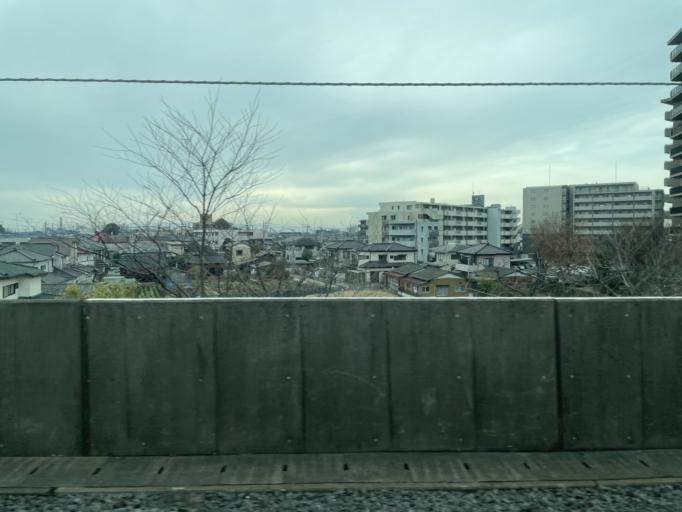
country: JP
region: Ibaraki
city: Koga
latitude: 36.1900
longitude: 139.7108
